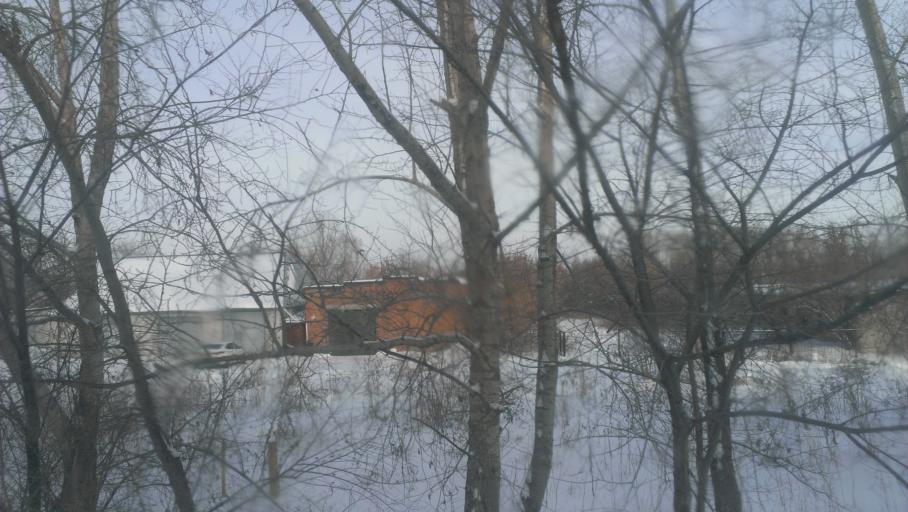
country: RU
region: Altai Krai
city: Nauchnyy Gorodok
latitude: 53.4208
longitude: 83.5230
